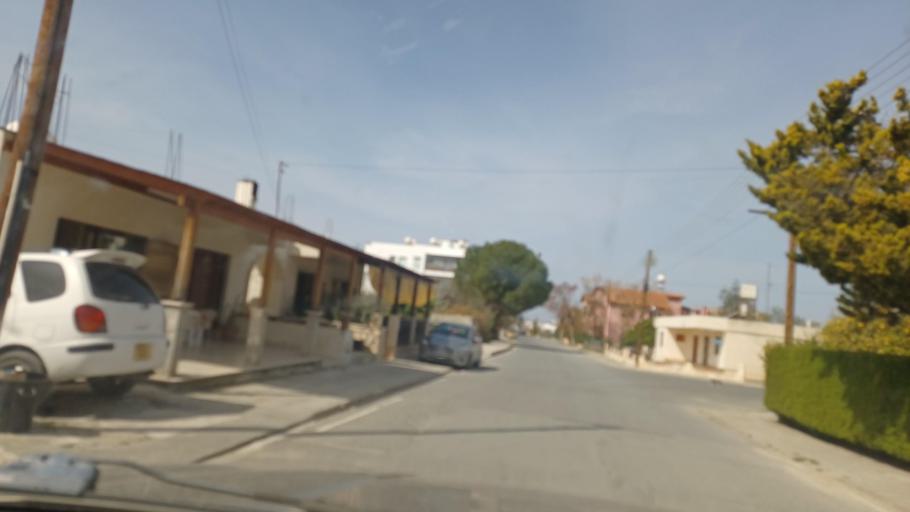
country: CY
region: Pafos
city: Paphos
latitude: 34.7593
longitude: 32.4617
